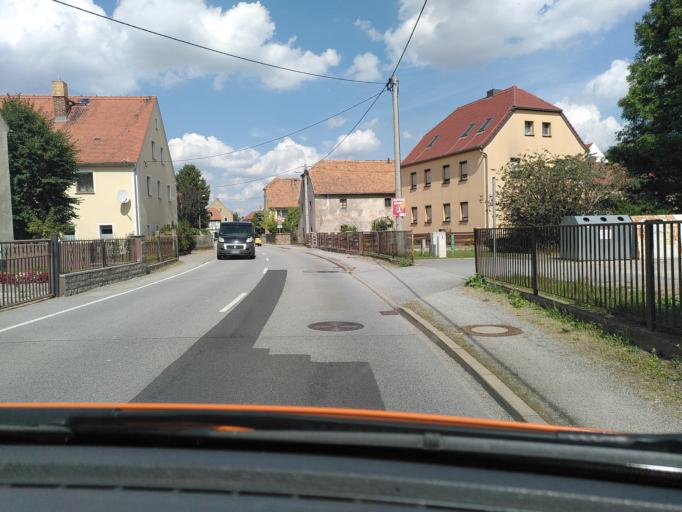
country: DE
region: Saxony
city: Grossdubrau
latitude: 51.2250
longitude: 14.4777
